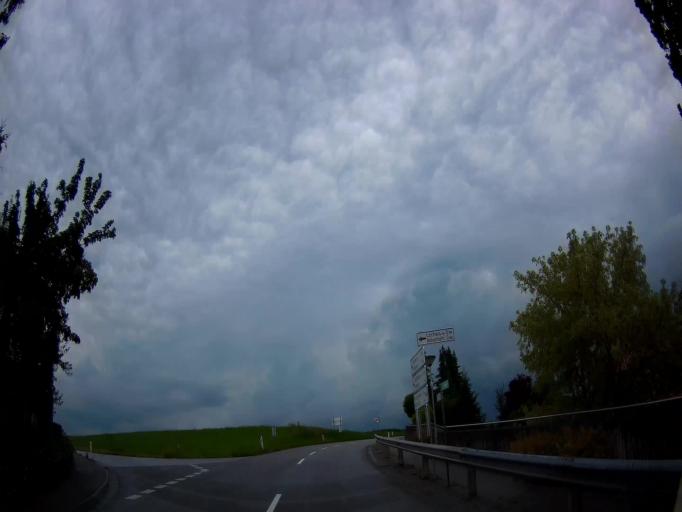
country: AT
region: Salzburg
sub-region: Politischer Bezirk Salzburg-Umgebung
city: Mattsee
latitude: 48.0467
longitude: 13.1501
